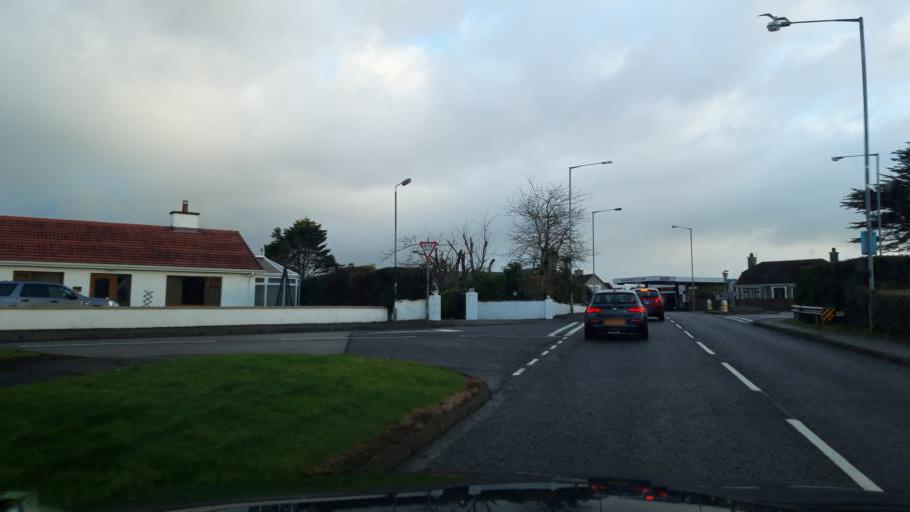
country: GB
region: Northern Ireland
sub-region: Moyle District
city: Ballycastle
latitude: 55.1965
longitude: -6.2630
